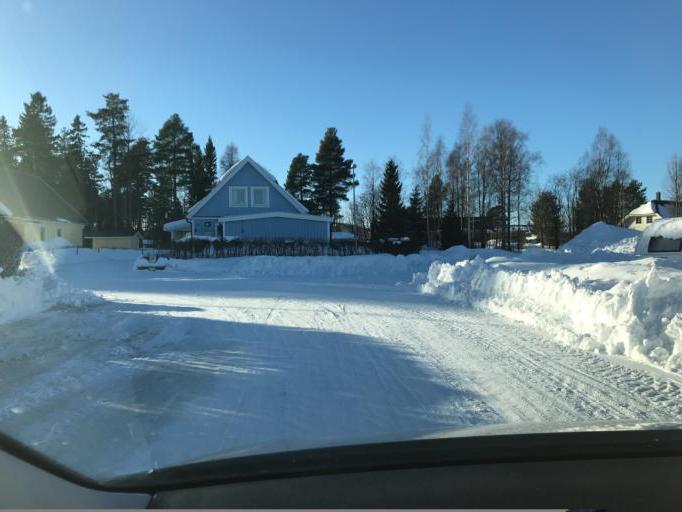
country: SE
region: Norrbotten
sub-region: Lulea Kommun
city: Sodra Sunderbyn
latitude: 65.6489
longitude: 21.9610
